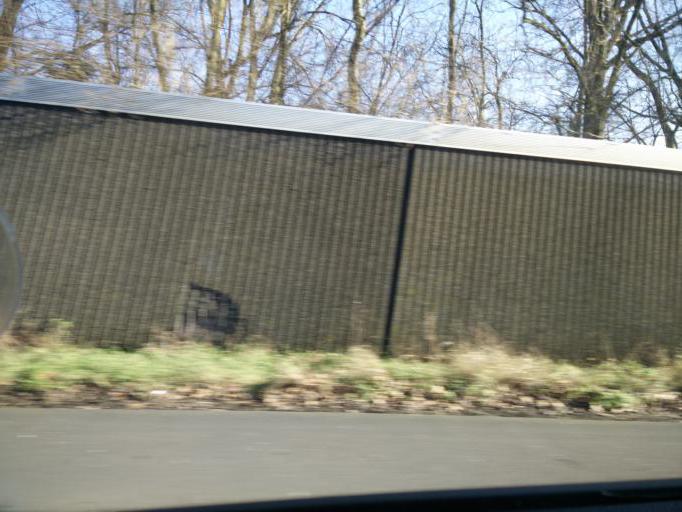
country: BE
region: Flanders
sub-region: Provincie Antwerpen
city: Kapellen
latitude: 51.2839
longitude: 4.4097
